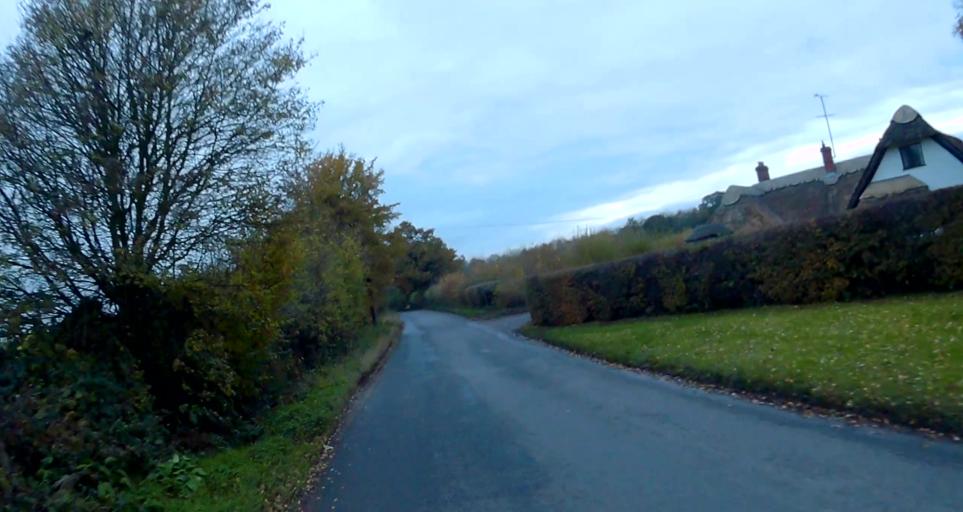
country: GB
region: England
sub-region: Hampshire
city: Odiham
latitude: 51.2371
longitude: -0.9873
